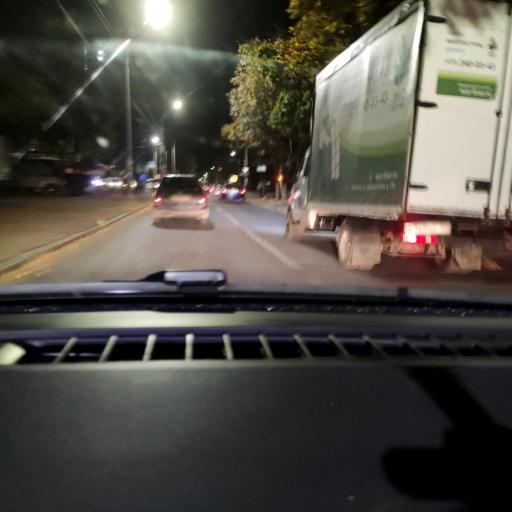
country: RU
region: Voronezj
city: Podgornoye
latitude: 51.7054
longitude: 39.1632
